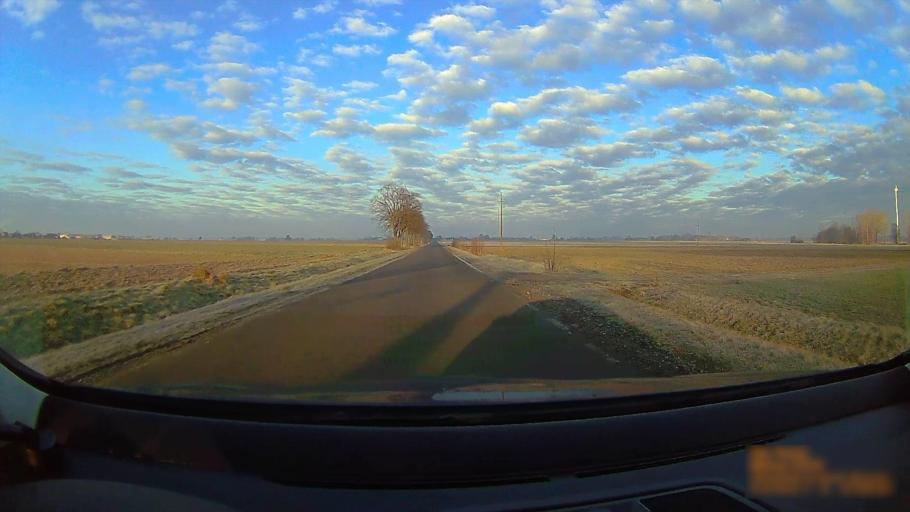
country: PL
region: Greater Poland Voivodeship
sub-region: Powiat koninski
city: Rychwal
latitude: 52.0964
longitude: 18.1355
